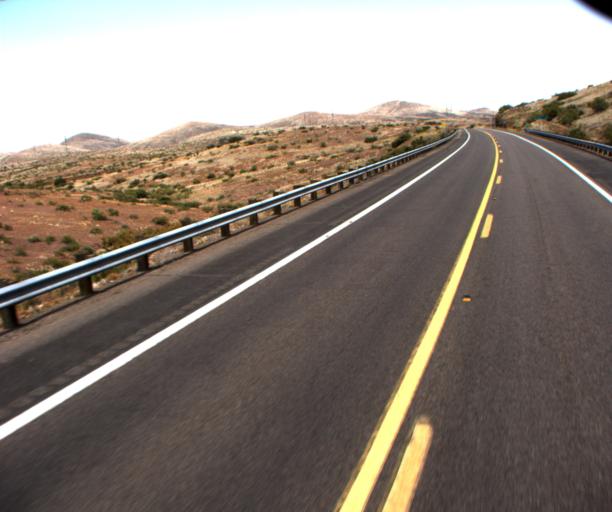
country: US
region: Arizona
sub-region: Greenlee County
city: Clifton
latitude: 32.7505
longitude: -109.2346
